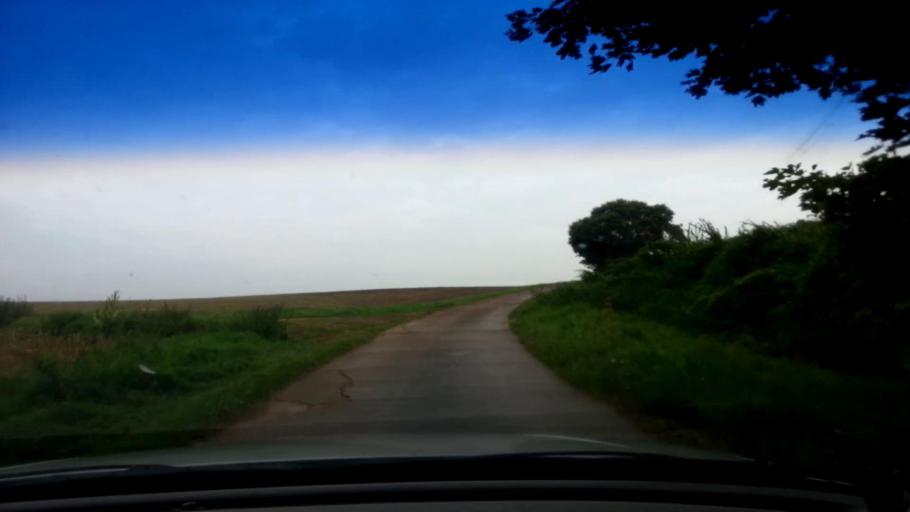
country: DE
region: Bavaria
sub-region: Upper Franconia
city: Rattelsdorf
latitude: 50.0591
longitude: 10.8832
